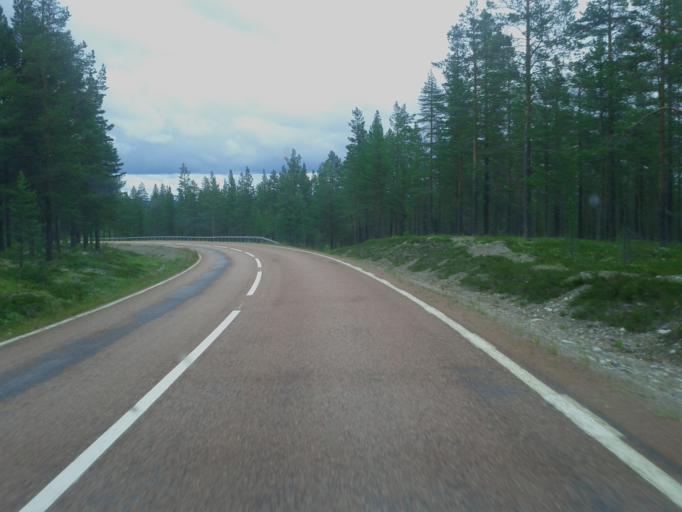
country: NO
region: Hedmark
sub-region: Engerdal
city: Engerdal
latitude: 61.8040
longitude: 12.4038
